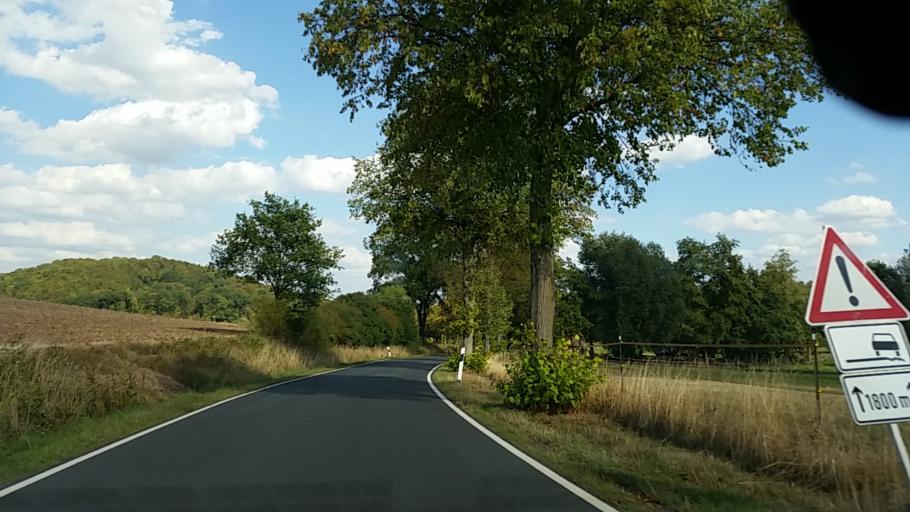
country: DE
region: Lower Saxony
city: Juhnde
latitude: 51.4221
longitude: 9.8134
